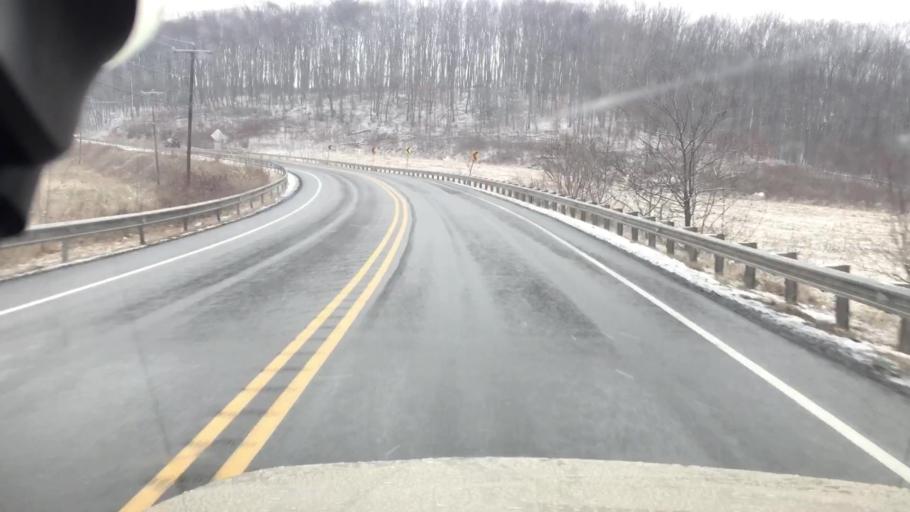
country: US
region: Pennsylvania
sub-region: Luzerne County
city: Nescopeck
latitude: 41.0539
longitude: -76.1749
